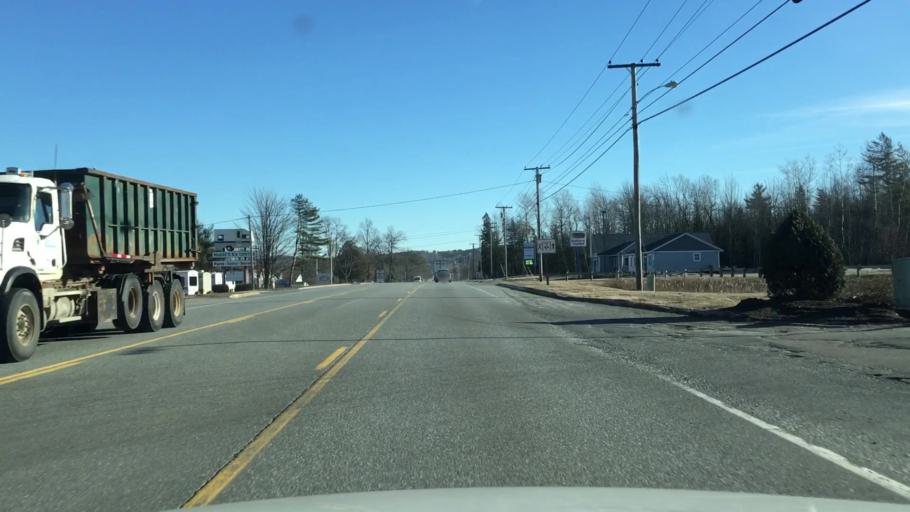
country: US
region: Maine
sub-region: Penobscot County
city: Holden
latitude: 44.7645
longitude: -68.7056
